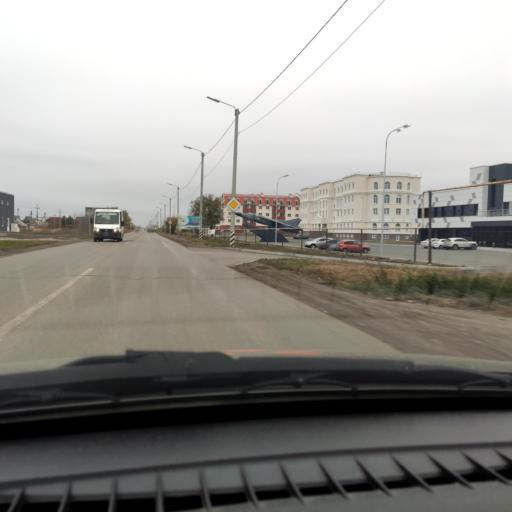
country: RU
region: Samara
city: Podstepki
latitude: 53.5216
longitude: 49.1931
